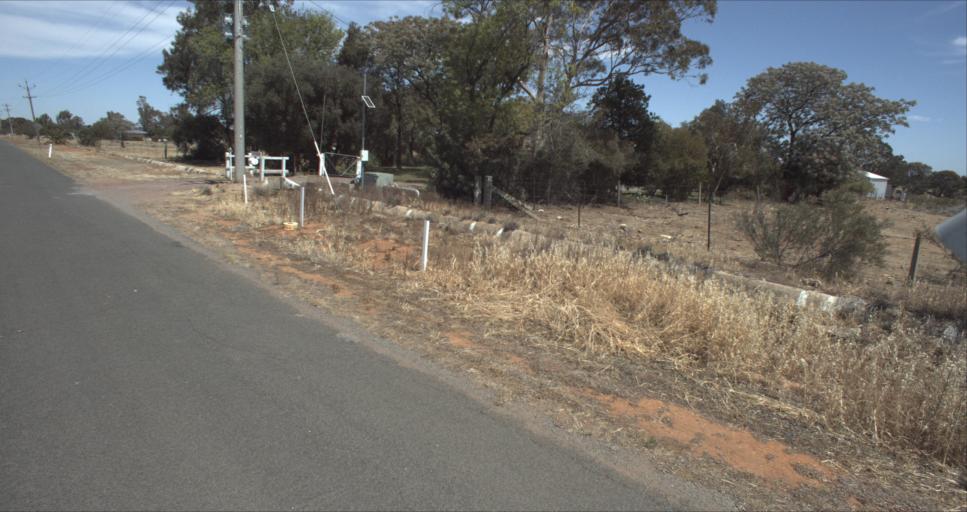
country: AU
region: New South Wales
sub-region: Leeton
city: Leeton
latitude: -34.5942
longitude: 146.4282
